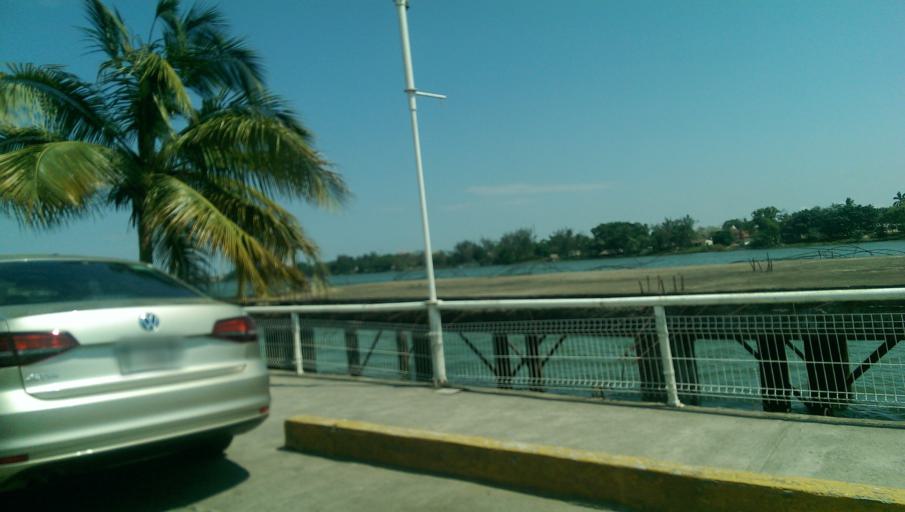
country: MX
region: Veracruz
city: Tuxpan de Rodriguez Cano
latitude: 20.9529
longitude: -97.4118
